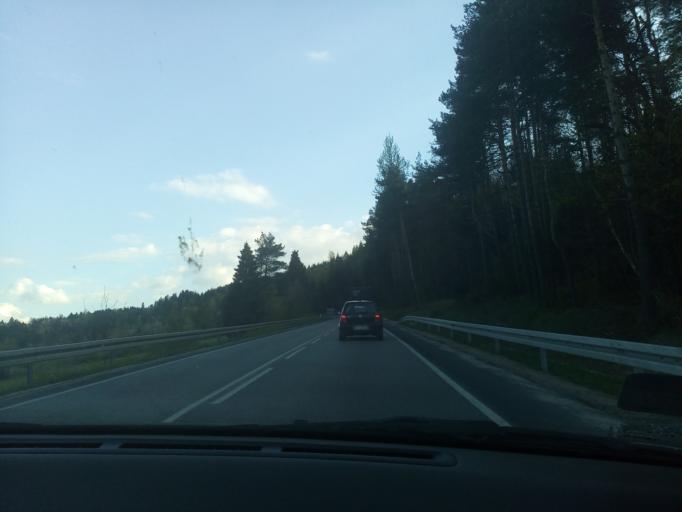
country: PL
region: Lesser Poland Voivodeship
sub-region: Powiat nowosadecki
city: Krynica-Zdroj
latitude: 49.4718
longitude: 20.9458
